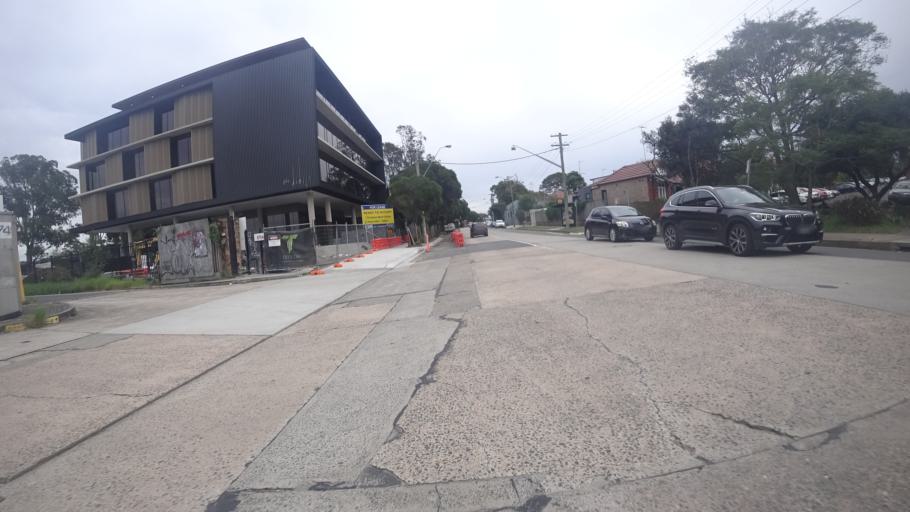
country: AU
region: New South Wales
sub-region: Marrickville
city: Newtown
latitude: -33.9078
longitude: 151.1701
